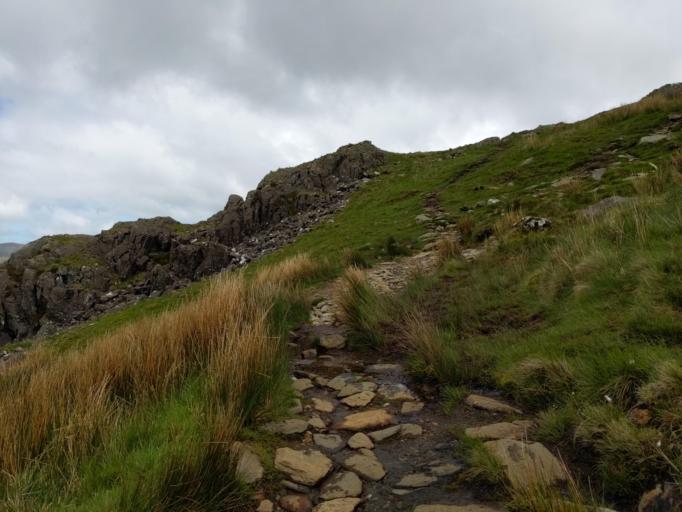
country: GB
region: Wales
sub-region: Gwynedd
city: Llanberis
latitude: 53.0591
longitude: -4.1022
